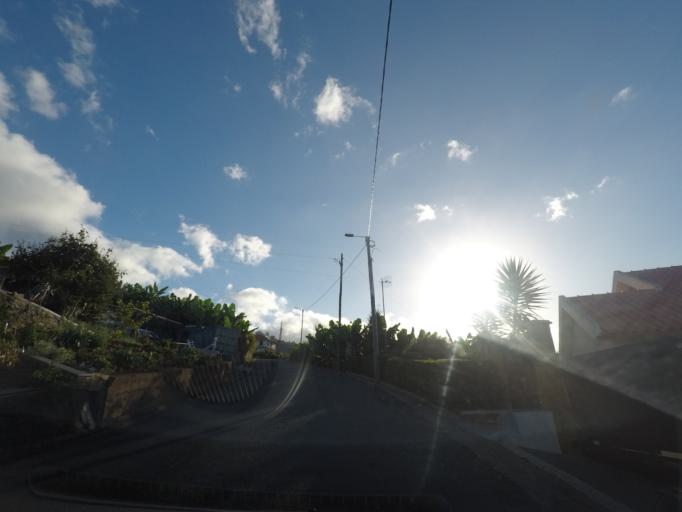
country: PT
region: Madeira
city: Ponta do Sol
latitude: 32.6881
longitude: -17.0889
